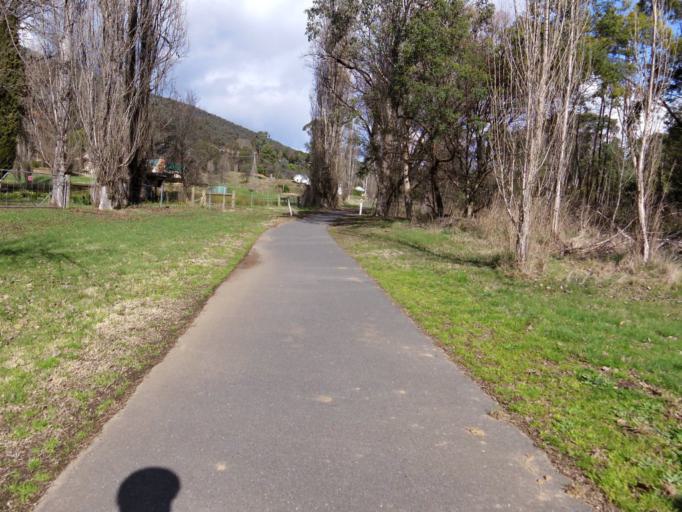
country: AU
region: Victoria
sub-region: Alpine
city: Mount Beauty
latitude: -36.7605
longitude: 146.9817
